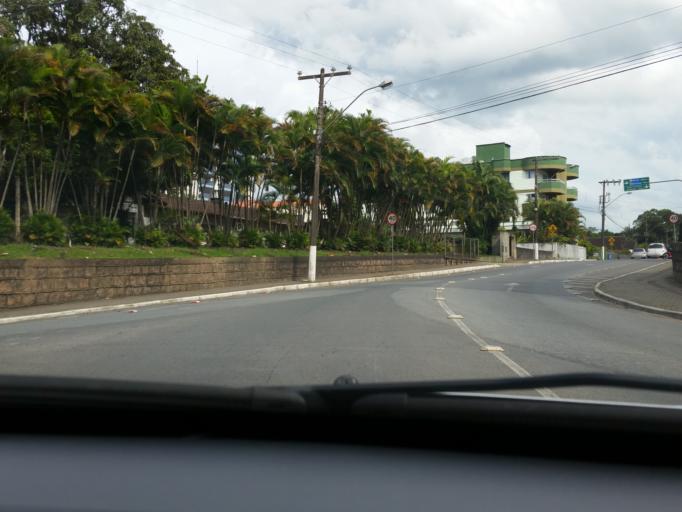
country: BR
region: Santa Catarina
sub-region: Indaial
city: Indaial
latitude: -26.8925
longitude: -49.2421
